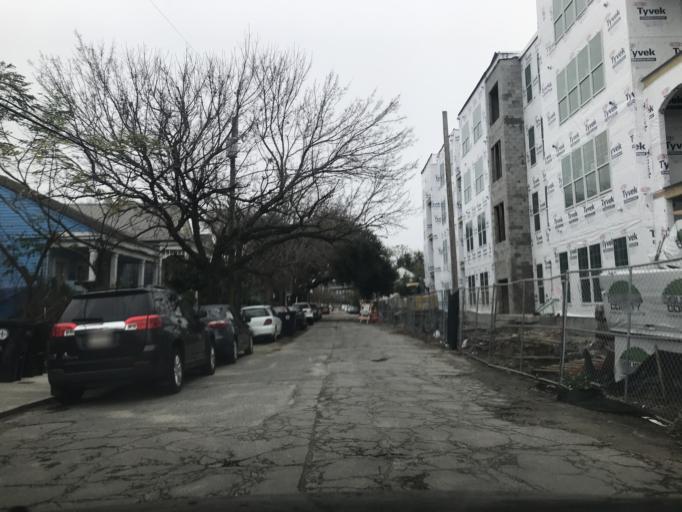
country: US
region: Louisiana
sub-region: Orleans Parish
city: New Orleans
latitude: 29.9371
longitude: -90.0704
